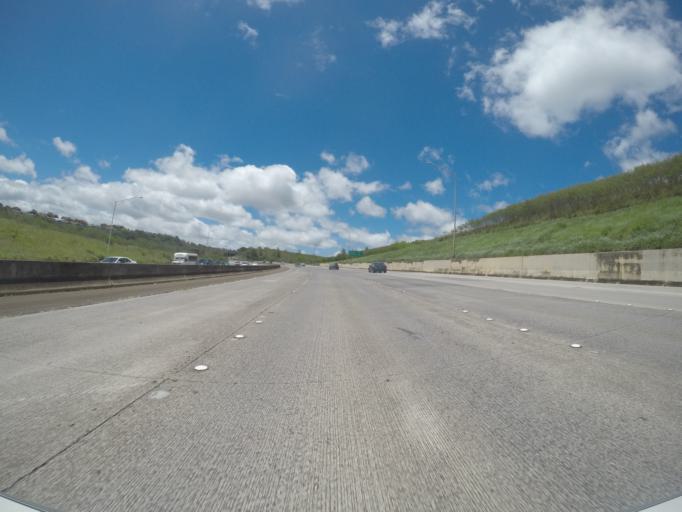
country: US
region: Hawaii
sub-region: Honolulu County
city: Waipio
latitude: 21.4108
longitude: -157.9895
